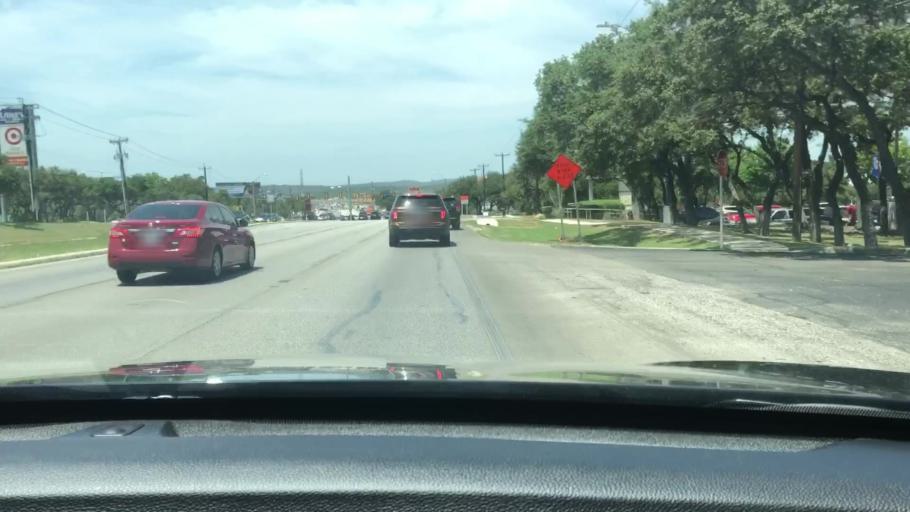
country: US
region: Texas
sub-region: Bexar County
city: Helotes
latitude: 29.5489
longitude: -98.6622
